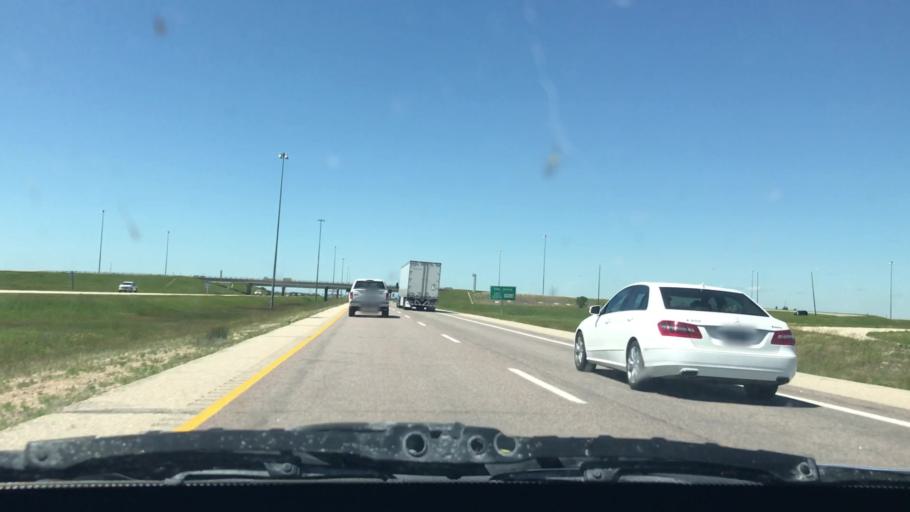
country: CA
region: Manitoba
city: Steinbach
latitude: 49.6990
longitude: -96.6403
